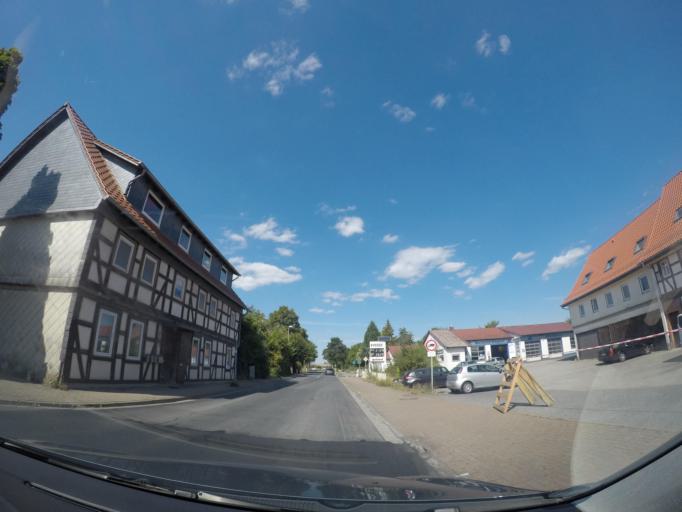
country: DE
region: Lower Saxony
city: Seesen
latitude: 51.8508
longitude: 10.1803
